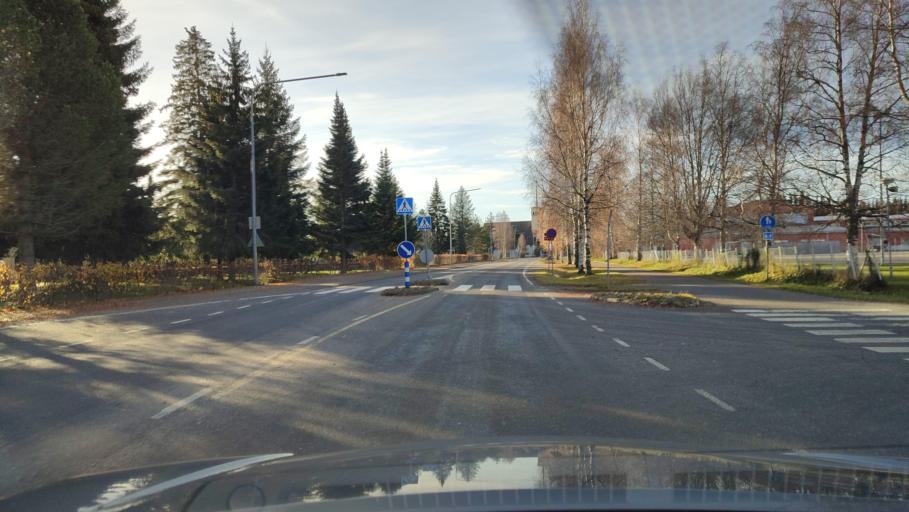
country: FI
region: Southern Ostrobothnia
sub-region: Suupohja
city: Teuva
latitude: 62.4816
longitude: 21.7432
